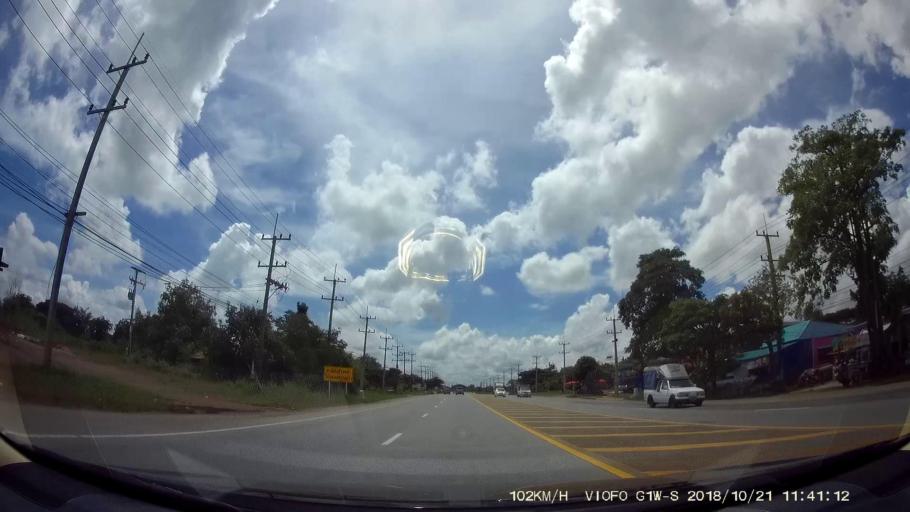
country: TH
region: Chaiyaphum
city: Chaiyaphum
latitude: 15.7023
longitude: 102.0148
